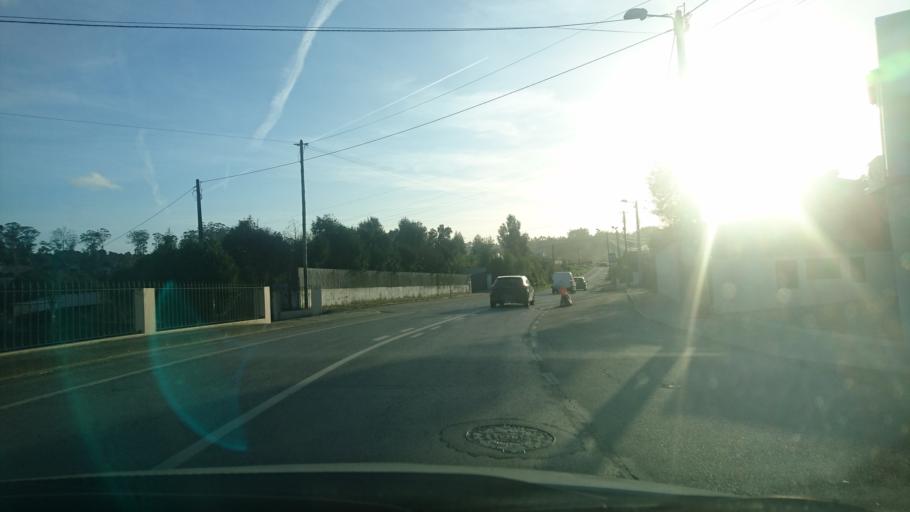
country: PT
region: Aveiro
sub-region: Santa Maria da Feira
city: Pacos de Brandao
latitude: 40.9815
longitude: -8.5984
